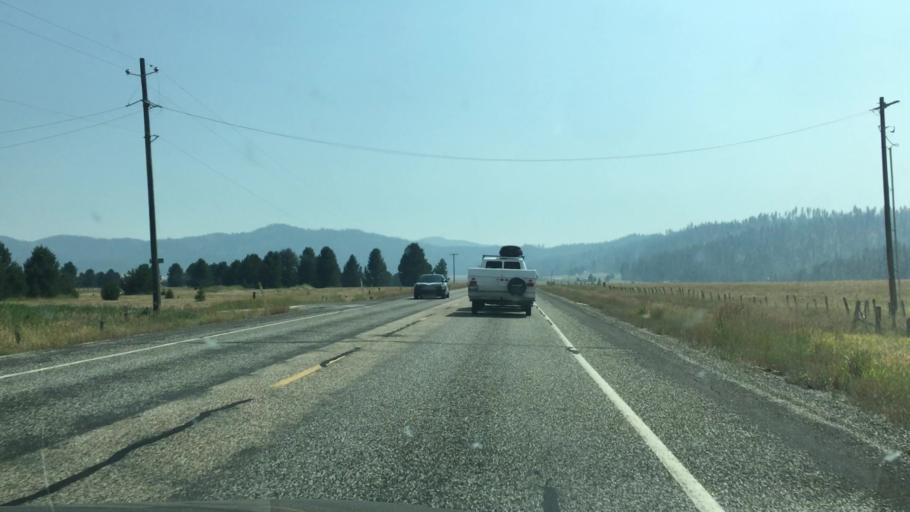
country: US
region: Idaho
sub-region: Valley County
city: Cascade
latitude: 44.3449
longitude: -116.0276
